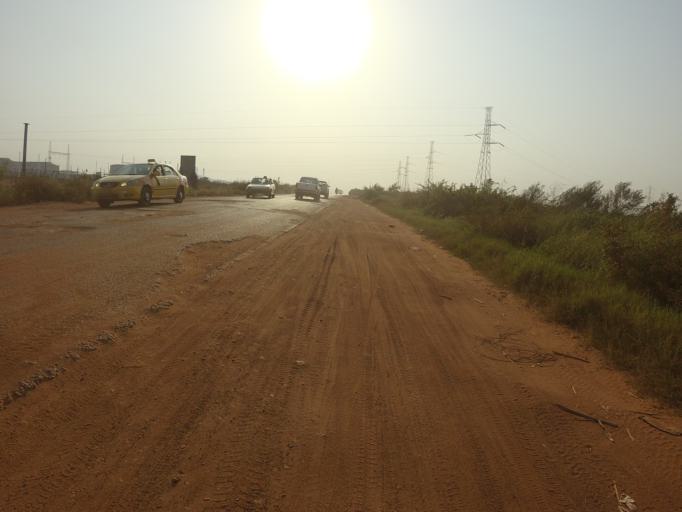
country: GH
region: Greater Accra
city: Tema
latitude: 5.6717
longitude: 0.0214
